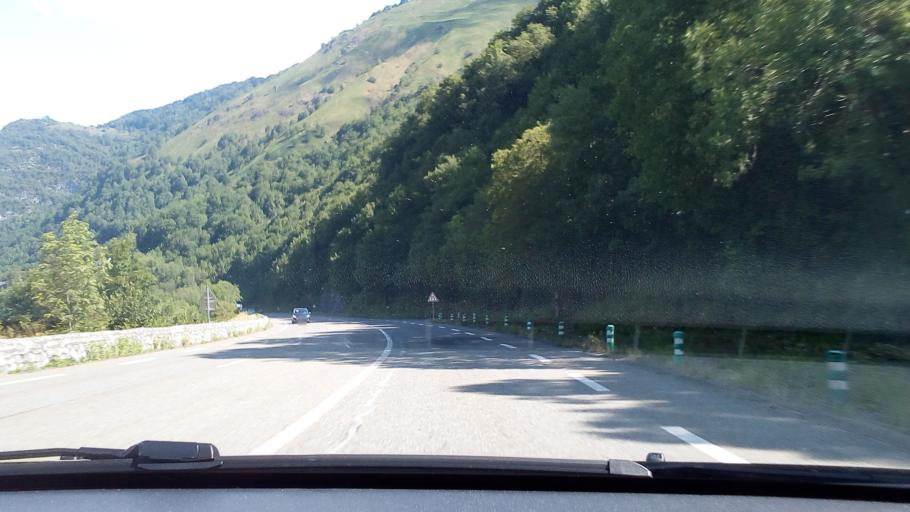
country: ES
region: Aragon
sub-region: Provincia de Huesca
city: Canfranc
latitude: 42.8631
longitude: -0.5500
